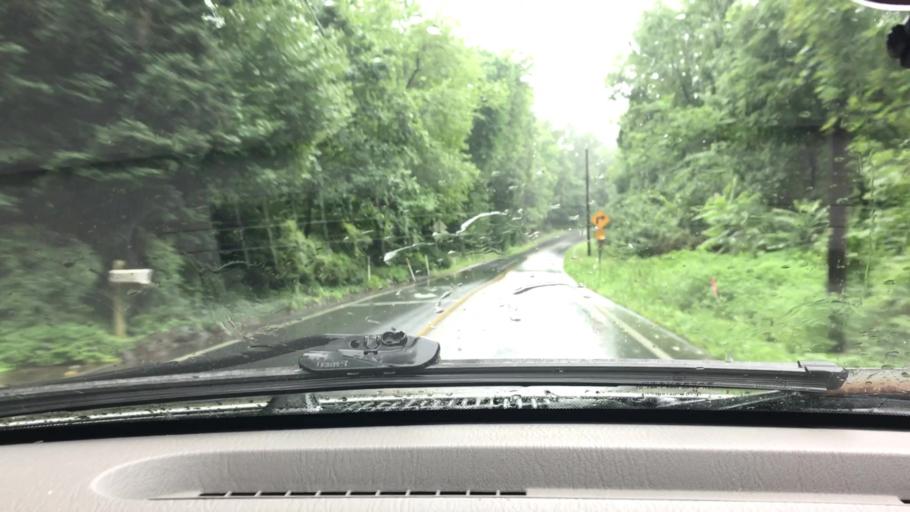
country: US
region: Pennsylvania
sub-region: Lancaster County
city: Elizabethtown
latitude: 40.1809
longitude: -76.5855
